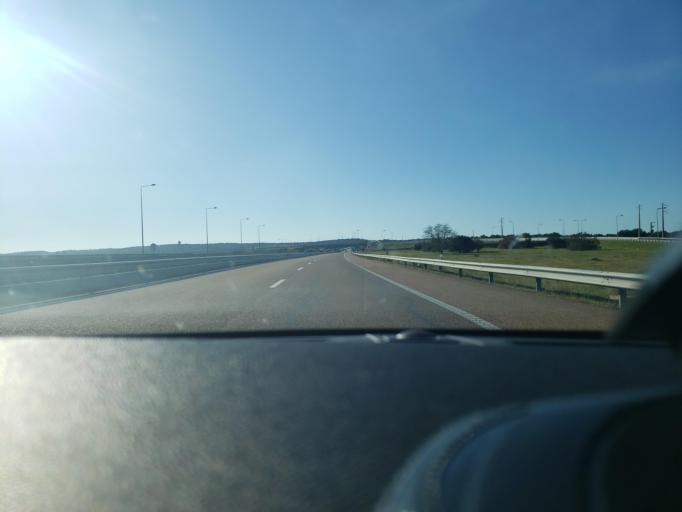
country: PT
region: Portalegre
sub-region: Elvas
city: Elvas
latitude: 38.8845
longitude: -7.2231
